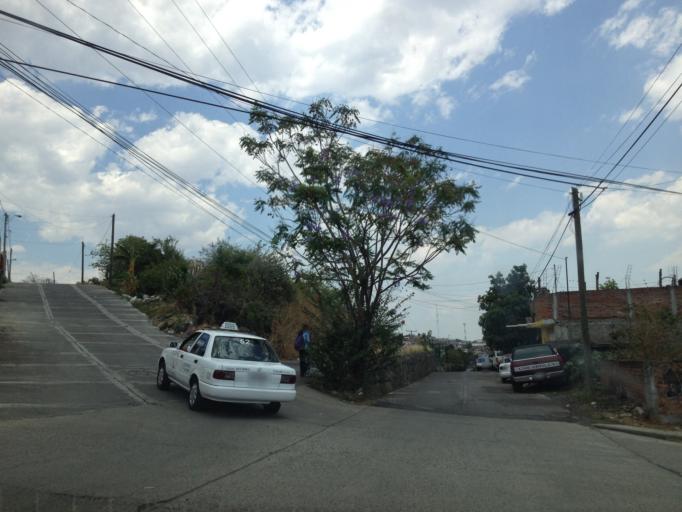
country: MX
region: Michoacan
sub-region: Morelia
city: San Antonio
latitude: 19.7049
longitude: -101.2463
